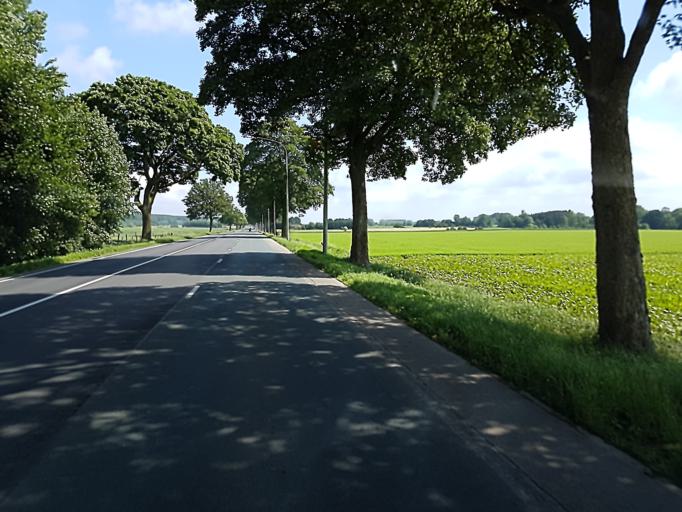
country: BE
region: Wallonia
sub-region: Province du Hainaut
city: Soignies
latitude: 50.5207
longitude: 4.0195
